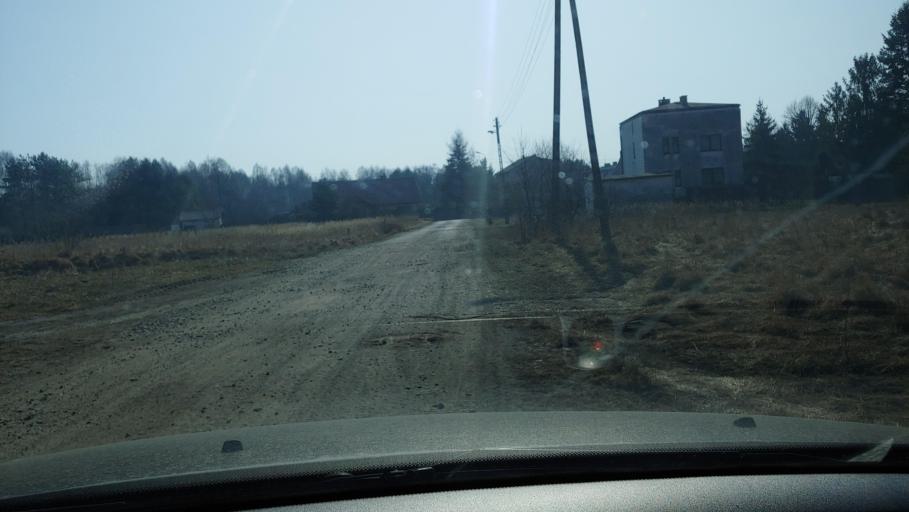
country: PL
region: Lesser Poland Voivodeship
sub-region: Powiat chrzanowski
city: Luszowice
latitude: 50.1555
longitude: 19.4306
